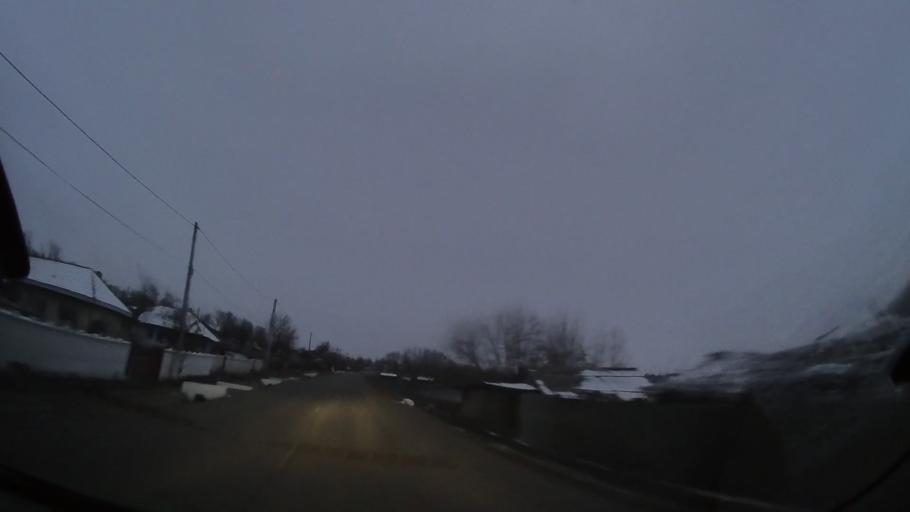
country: RO
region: Vaslui
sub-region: Comuna Vutcani
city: Vutcani
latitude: 46.4534
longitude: 28.0212
